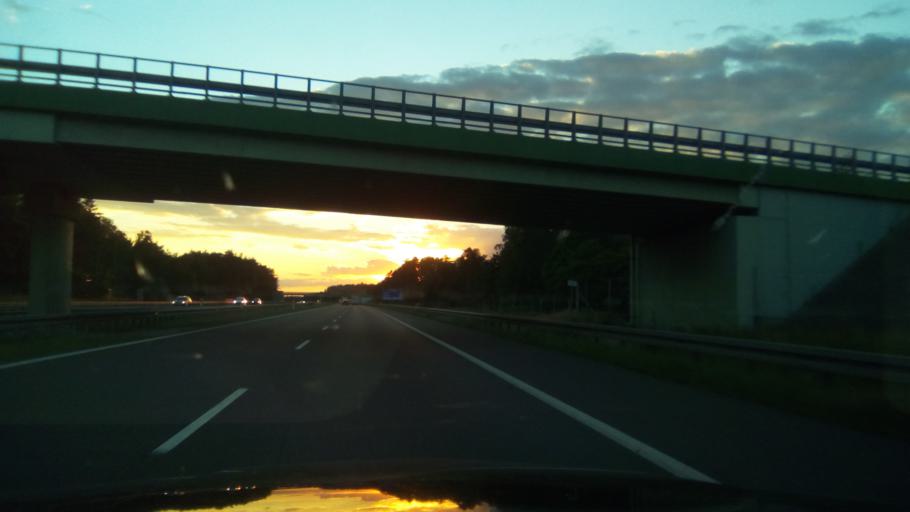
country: PL
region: Lodz Voivodeship
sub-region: Powiat zgierski
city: Zgierz
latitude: 51.9121
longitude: 19.4339
